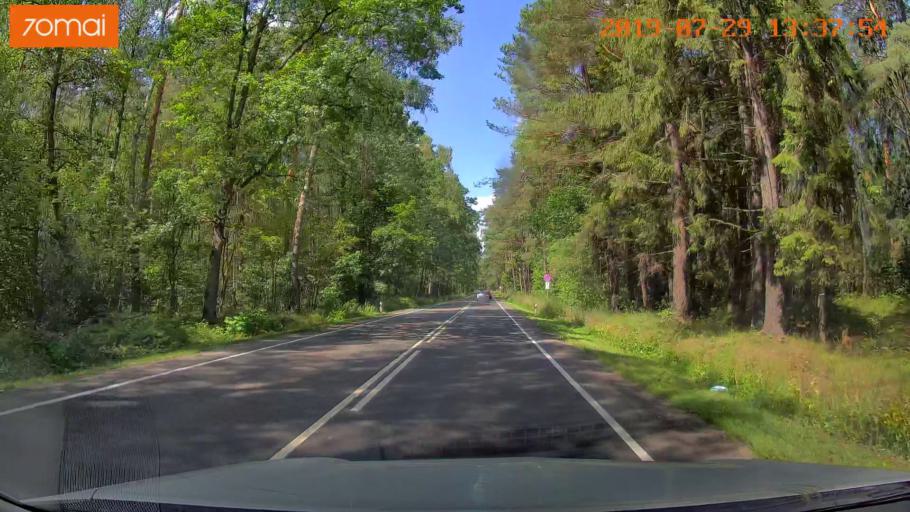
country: RU
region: Kaliningrad
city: Volochayevskoye
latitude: 54.7173
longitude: 20.1777
